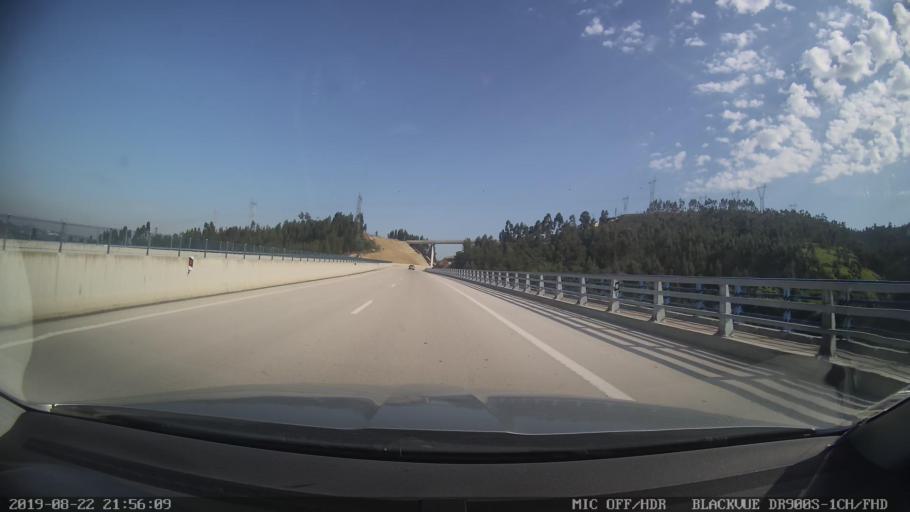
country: PT
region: Coimbra
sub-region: Coimbra
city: Coimbra
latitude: 40.1652
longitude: -8.3784
